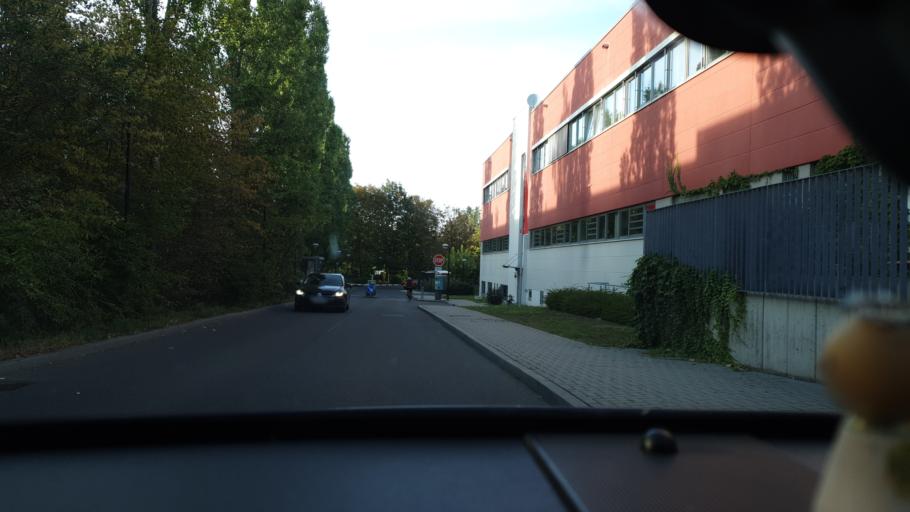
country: DE
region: Saxony
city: Rackwitz
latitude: 51.3863
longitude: 12.3787
